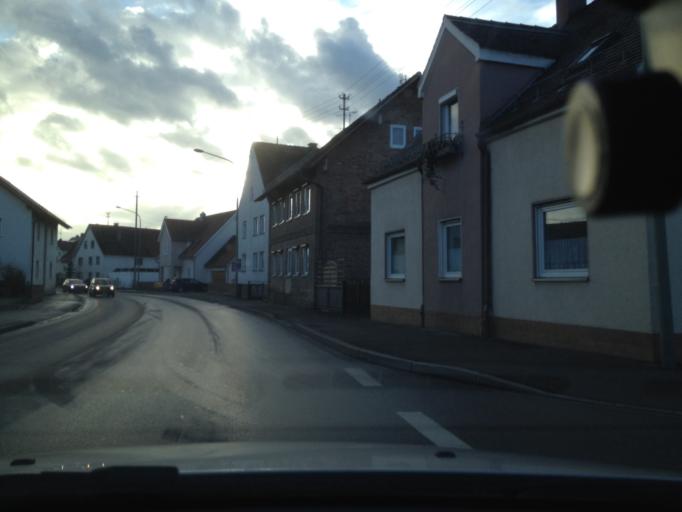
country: DE
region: Bavaria
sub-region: Swabia
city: Schwabmunchen
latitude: 48.1755
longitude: 10.7571
